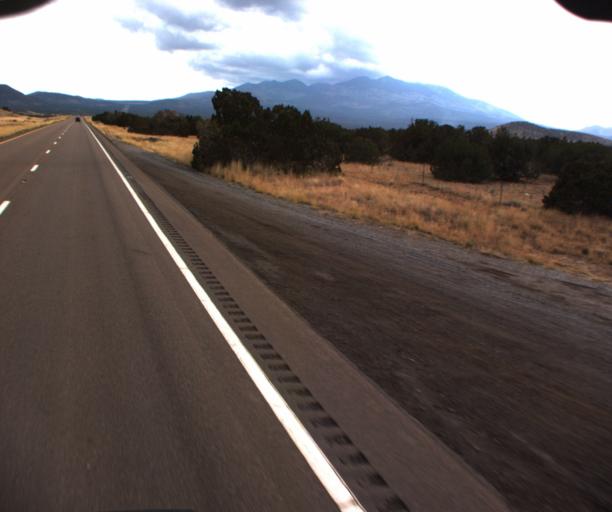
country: US
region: Arizona
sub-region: Coconino County
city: Flagstaff
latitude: 35.4761
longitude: -111.5575
